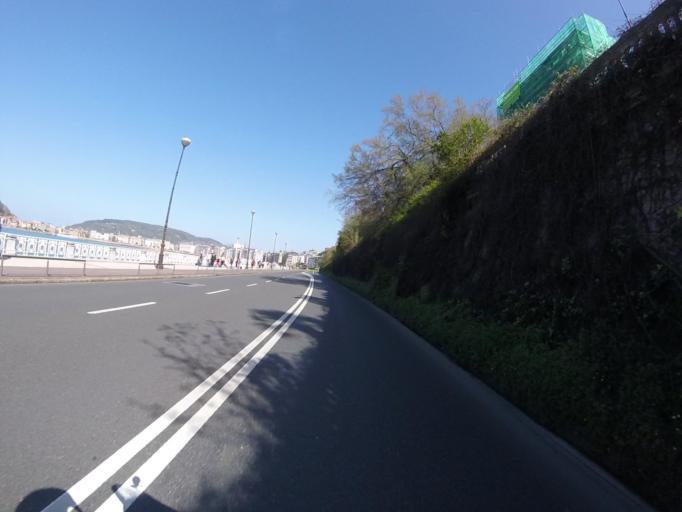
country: ES
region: Basque Country
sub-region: Provincia de Guipuzcoa
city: San Sebastian
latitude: 43.3144
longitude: -1.9959
